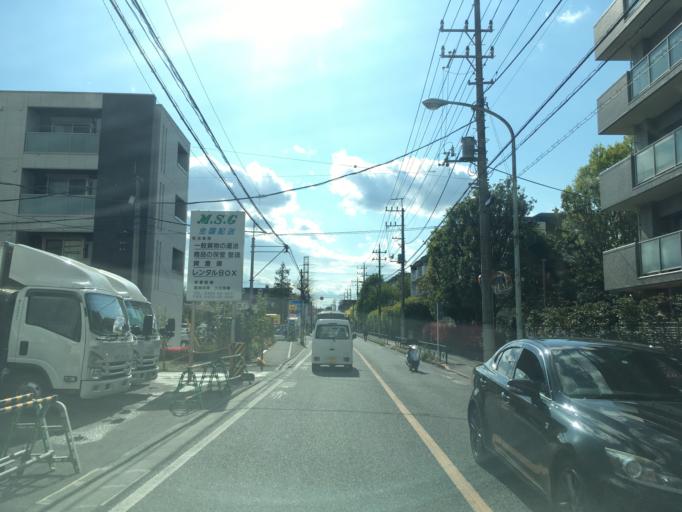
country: JP
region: Tokyo
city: Kamirenjaku
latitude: 35.6949
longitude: 139.5324
